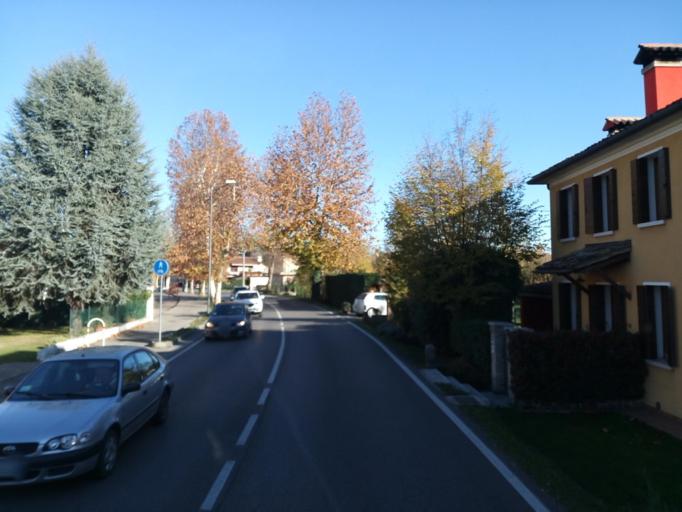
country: IT
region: Veneto
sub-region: Provincia di Treviso
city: Volpago del Montello
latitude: 45.7776
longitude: 12.1258
